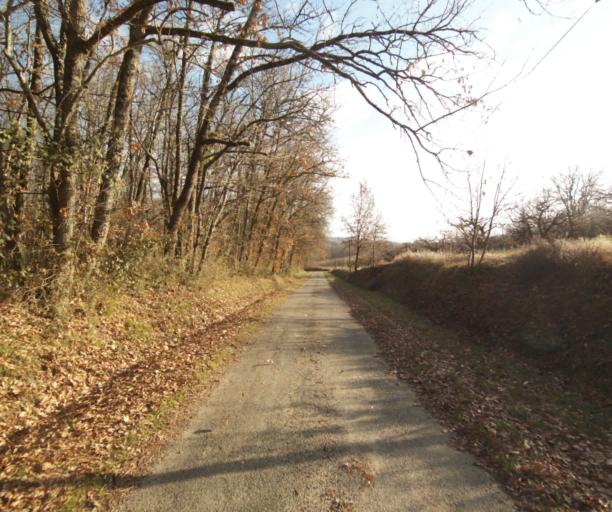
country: FR
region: Midi-Pyrenees
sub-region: Departement du Tarn-et-Garonne
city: Moissac
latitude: 44.1244
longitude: 1.0411
